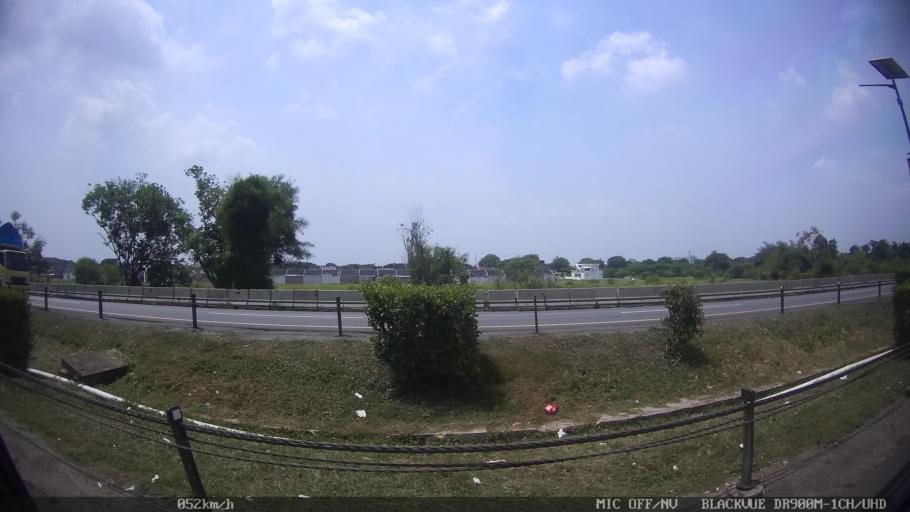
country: ID
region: Banten
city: Serang
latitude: -6.1288
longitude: 106.1952
